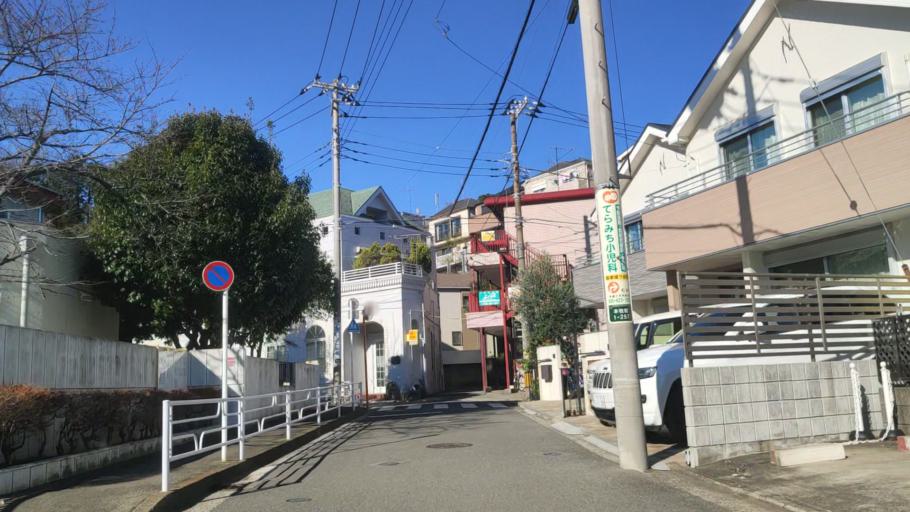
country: JP
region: Kanagawa
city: Yokohama
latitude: 35.4277
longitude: 139.6570
